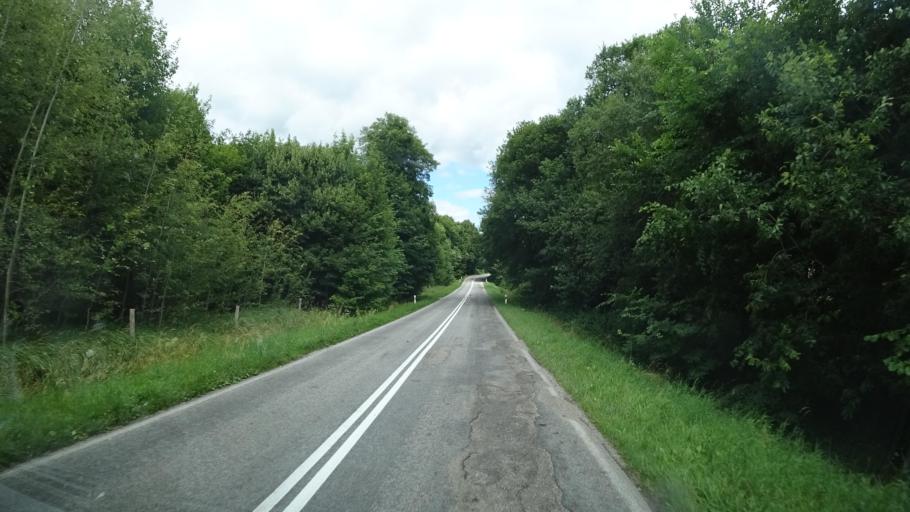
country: PL
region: Warmian-Masurian Voivodeship
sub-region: Powiat goldapski
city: Goldap
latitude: 54.2096
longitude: 22.2029
